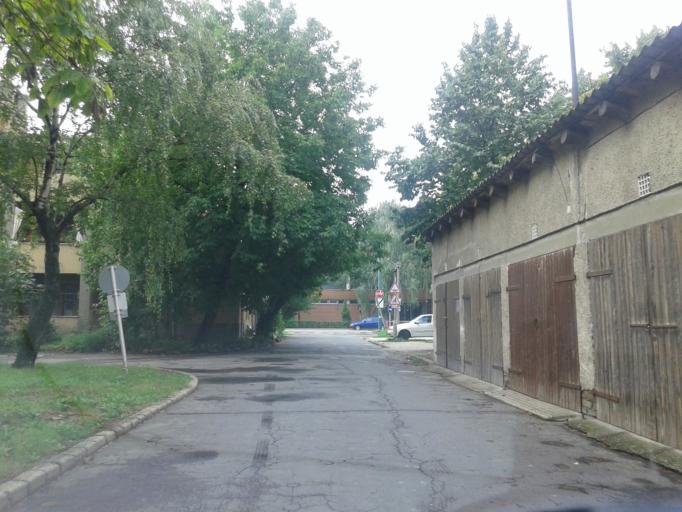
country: HU
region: Csongrad
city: Szeged
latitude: 46.2539
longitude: 20.1270
